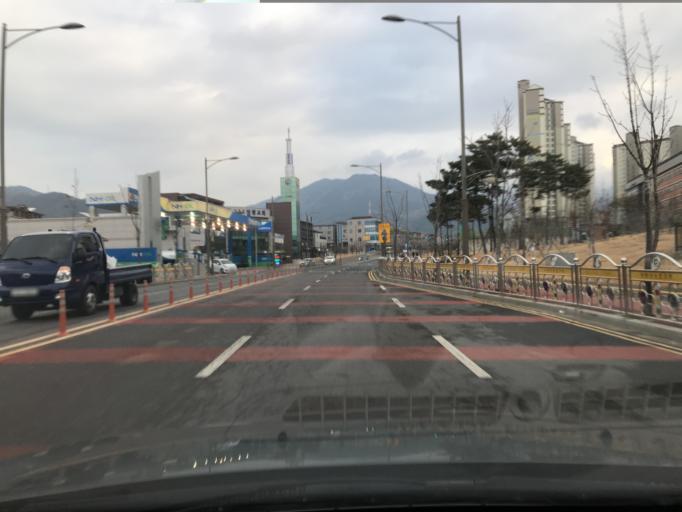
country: KR
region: Daegu
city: Hwawon
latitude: 35.6955
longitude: 128.4519
